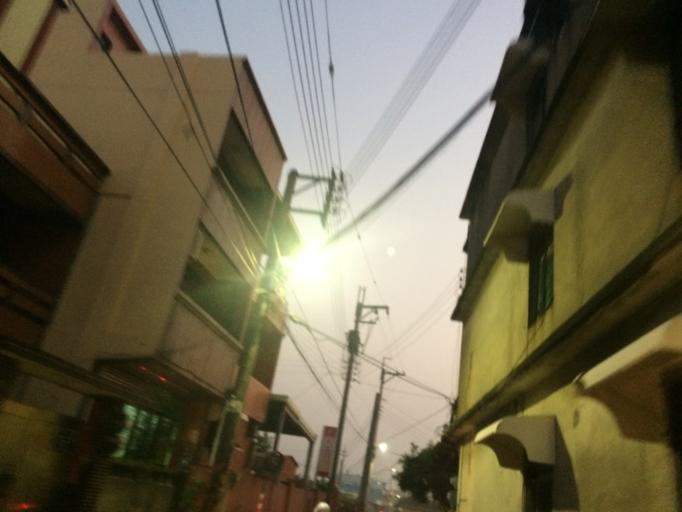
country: TW
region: Taiwan
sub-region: Hsinchu
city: Hsinchu
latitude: 24.7738
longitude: 120.9155
